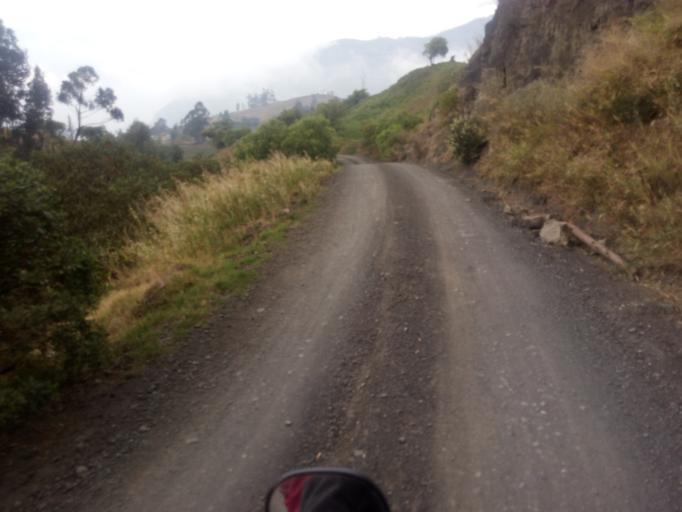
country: CO
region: Boyaca
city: Chita
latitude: 6.1936
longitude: -72.4864
